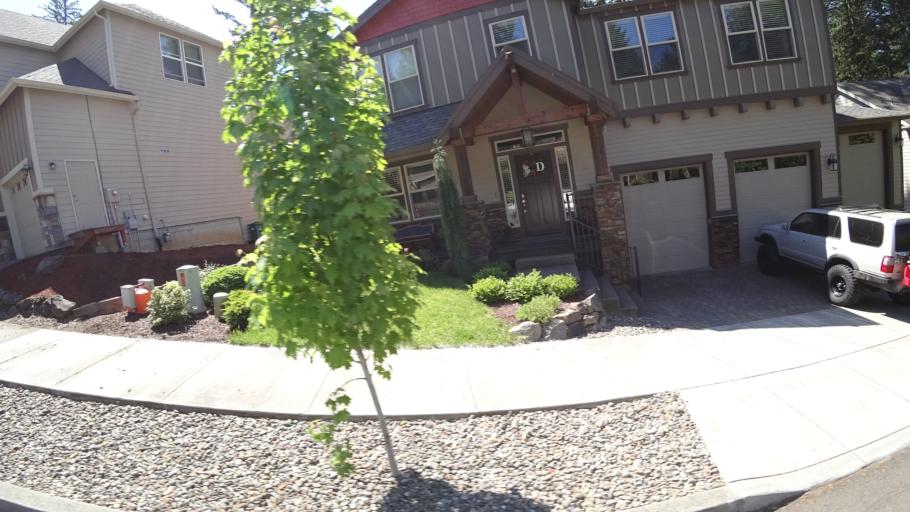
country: US
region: Oregon
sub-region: Clackamas County
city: Happy Valley
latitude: 45.4635
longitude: -122.5218
